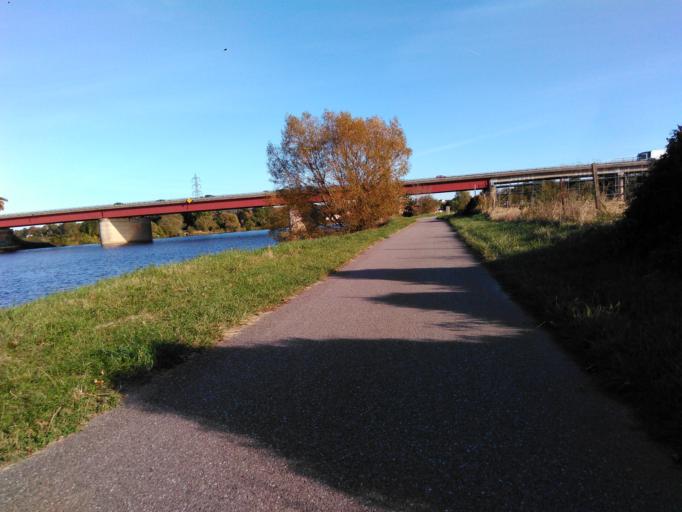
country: FR
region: Lorraine
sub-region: Departement de la Moselle
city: Bertrange
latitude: 49.2944
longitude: 6.1766
